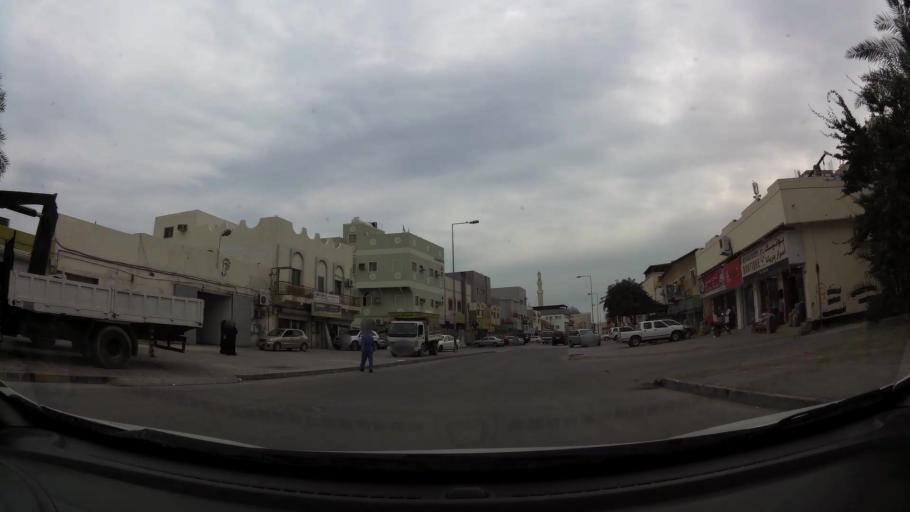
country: BH
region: Northern
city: Sitrah
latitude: 26.1646
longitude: 50.6141
